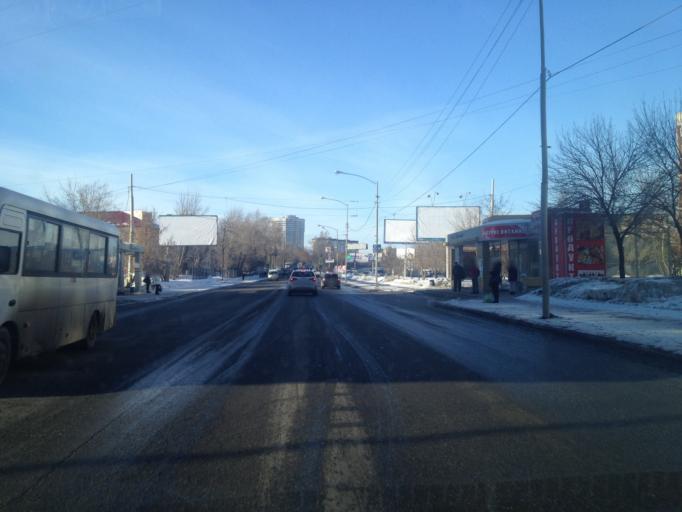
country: RU
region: Sverdlovsk
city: Yekaterinburg
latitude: 56.8549
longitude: 60.5534
